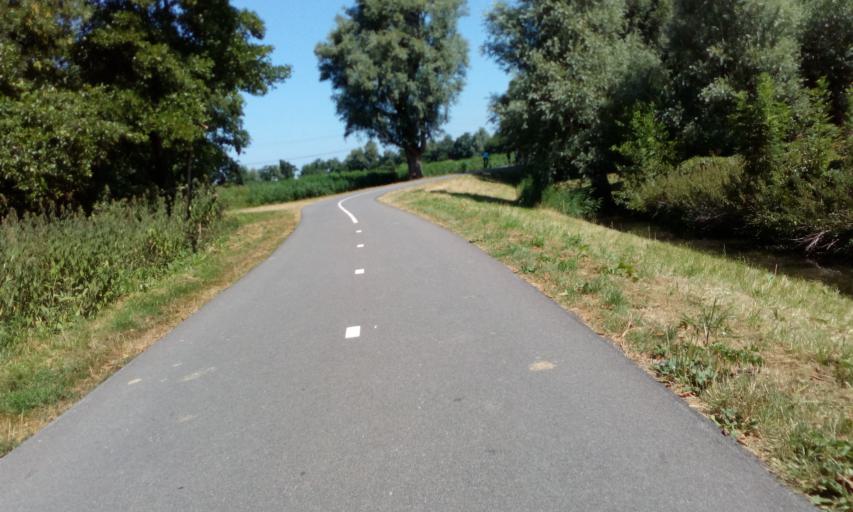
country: NL
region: South Holland
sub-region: Gemeente Westland
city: De Lier
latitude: 51.9902
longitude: 4.2584
